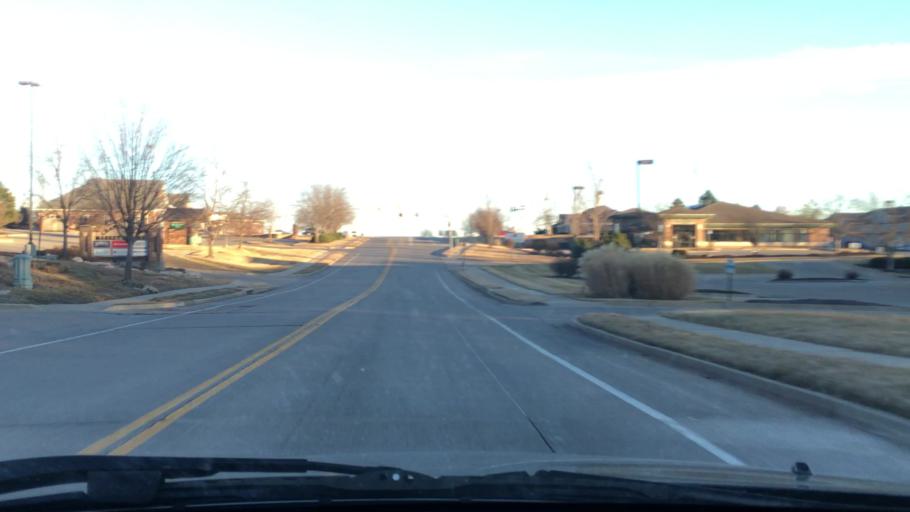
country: US
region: Missouri
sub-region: Boone County
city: Columbia
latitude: 38.9310
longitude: -92.3650
